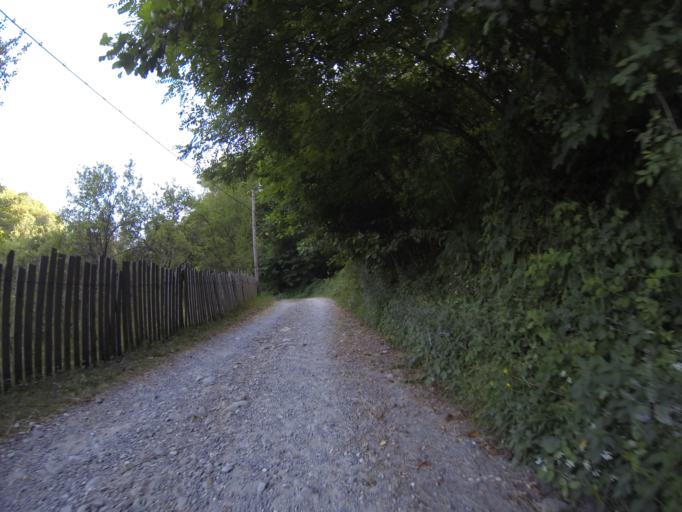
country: RO
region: Valcea
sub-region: Comuna Horezu
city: Horezu
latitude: 45.1816
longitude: 23.9923
